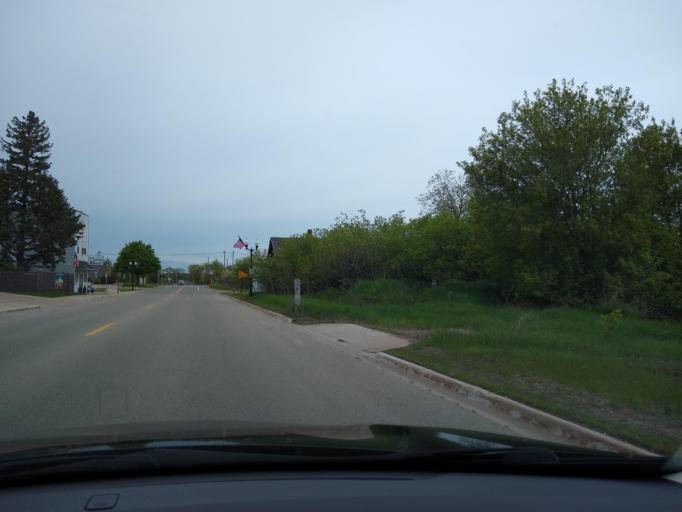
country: US
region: Michigan
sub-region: Delta County
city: Escanaba
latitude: 45.7664
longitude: -87.0691
